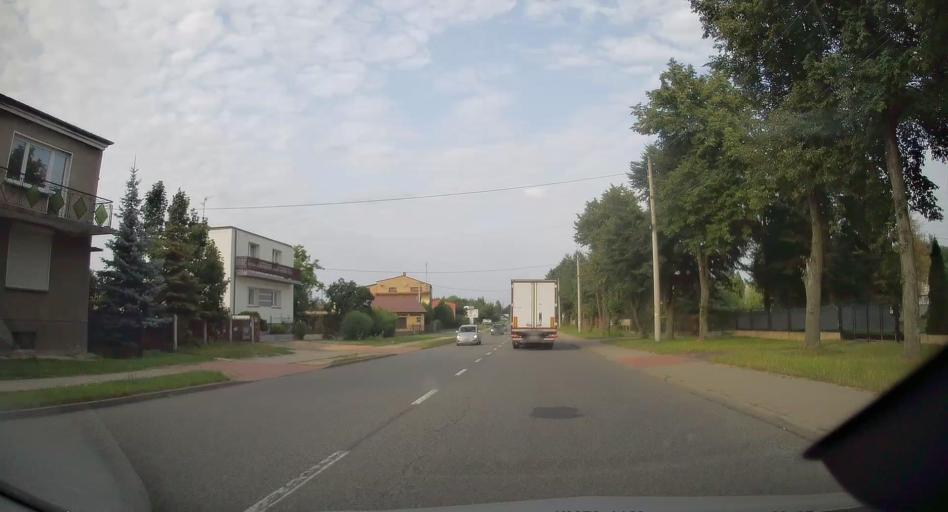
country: PL
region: Silesian Voivodeship
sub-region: Powiat czestochowski
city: Redziny
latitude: 50.8631
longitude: 19.2230
